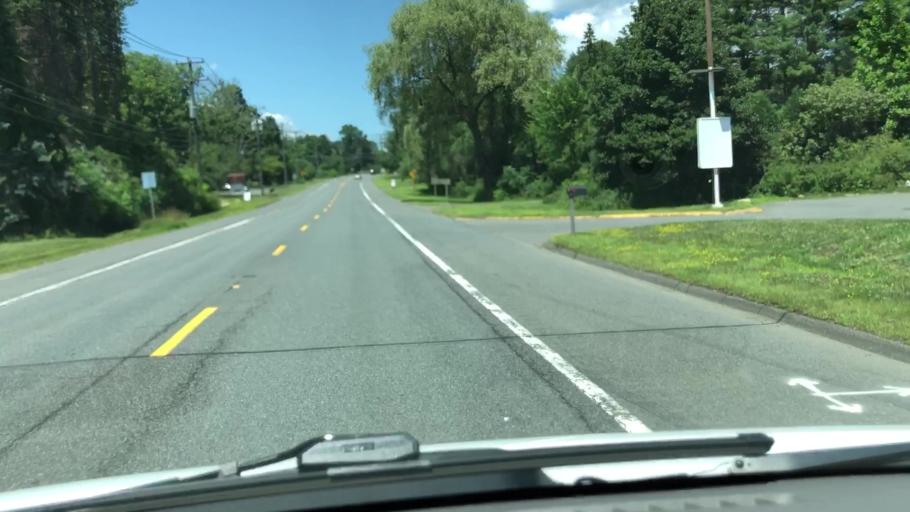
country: US
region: Massachusetts
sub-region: Hampshire County
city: North Amherst
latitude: 42.4306
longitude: -72.5428
